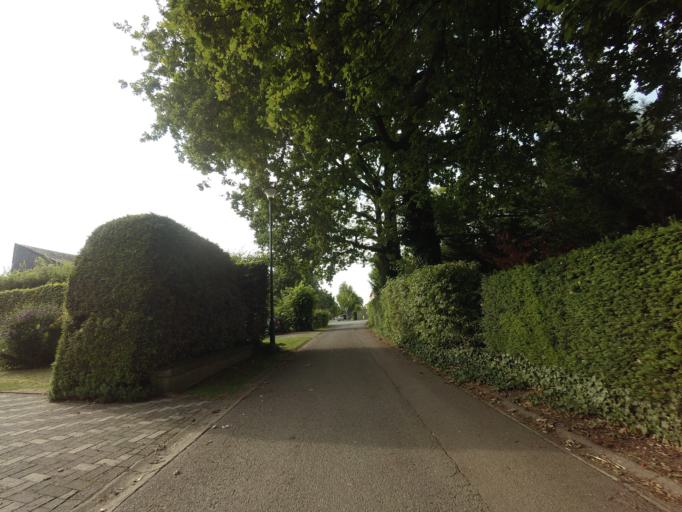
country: BE
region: Flanders
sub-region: Provincie Vlaams-Brabant
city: Diegem
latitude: 50.8870
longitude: 4.4378
